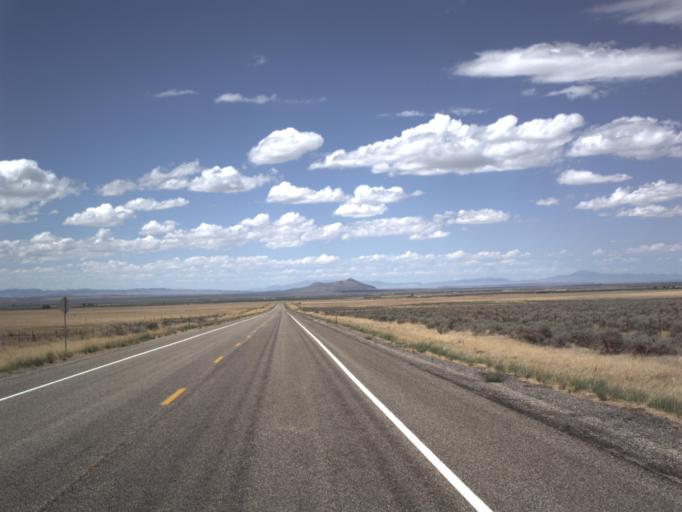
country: US
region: Utah
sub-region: Millard County
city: Fillmore
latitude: 39.1143
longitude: -112.2800
